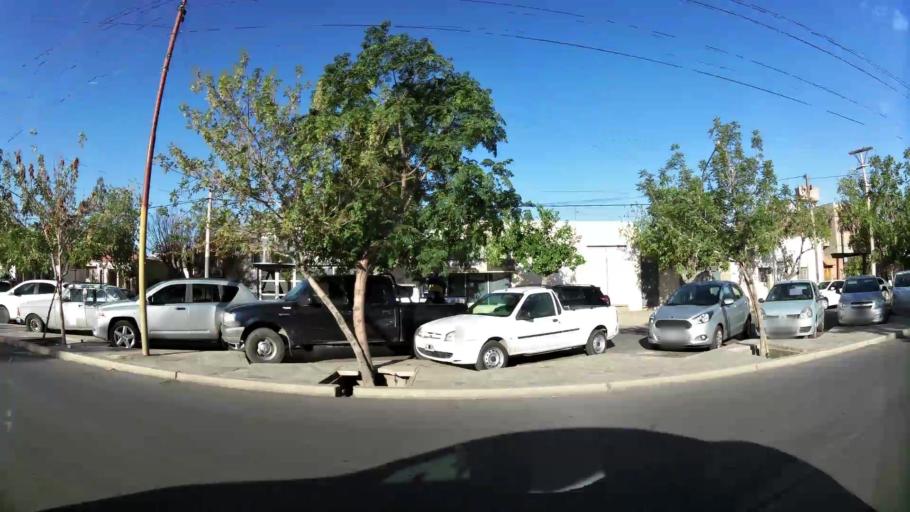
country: AR
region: San Juan
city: San Juan
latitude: -31.5432
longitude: -68.5208
